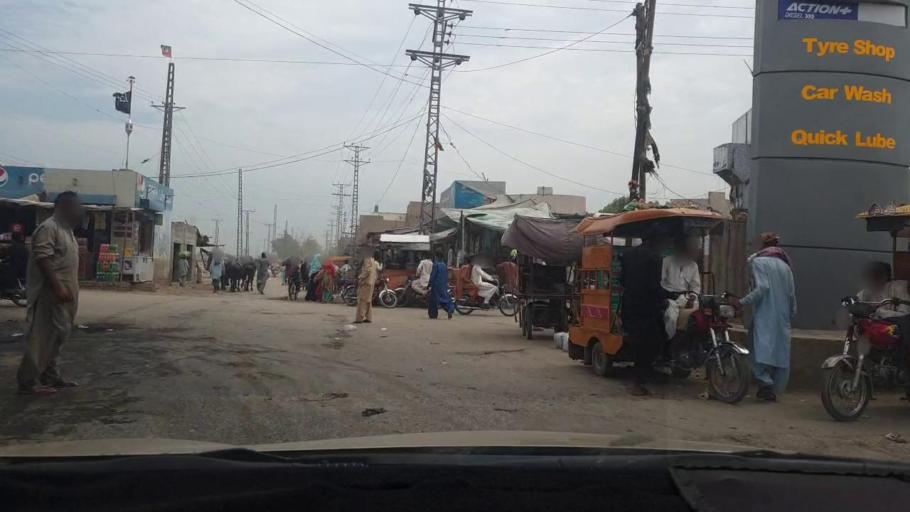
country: PK
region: Sindh
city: Naudero
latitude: 27.6711
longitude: 68.3569
